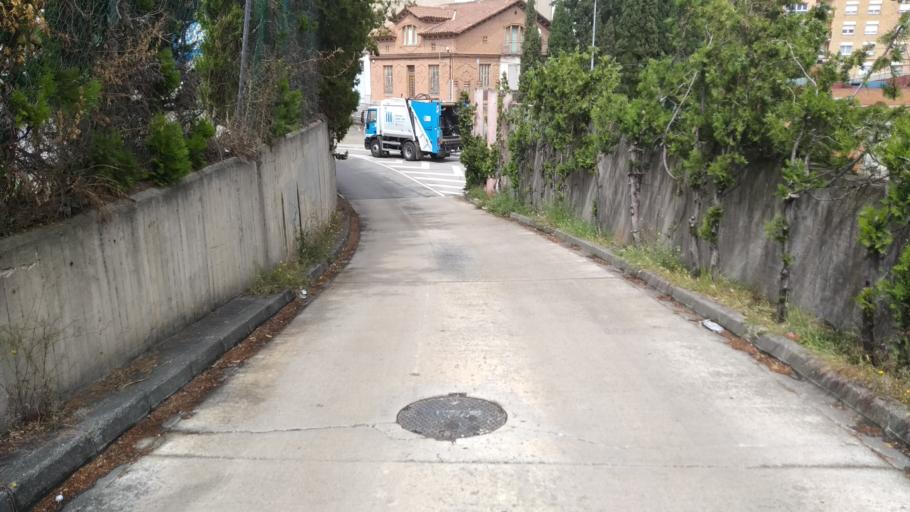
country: ES
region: Catalonia
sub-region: Provincia de Barcelona
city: Manresa
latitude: 41.7319
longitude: 1.8342
